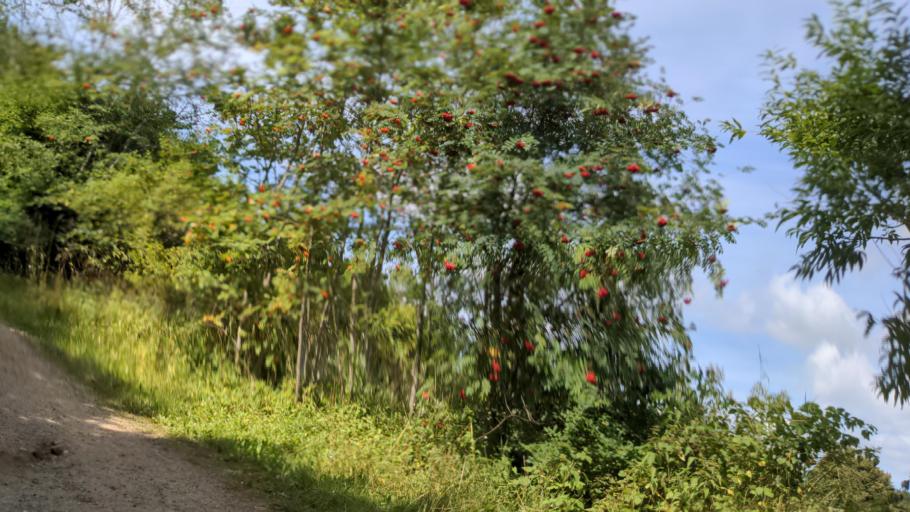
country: DE
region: Schleswig-Holstein
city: Eutin
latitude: 54.1494
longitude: 10.6089
